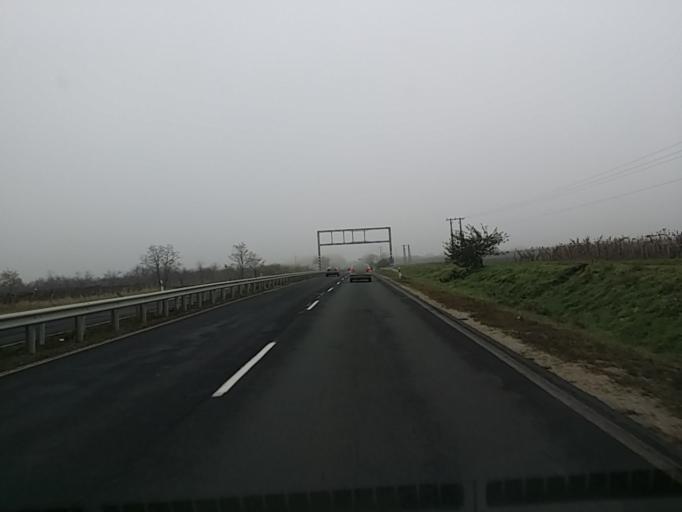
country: HU
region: Heves
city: Nagyrede
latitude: 47.7318
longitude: 19.8603
